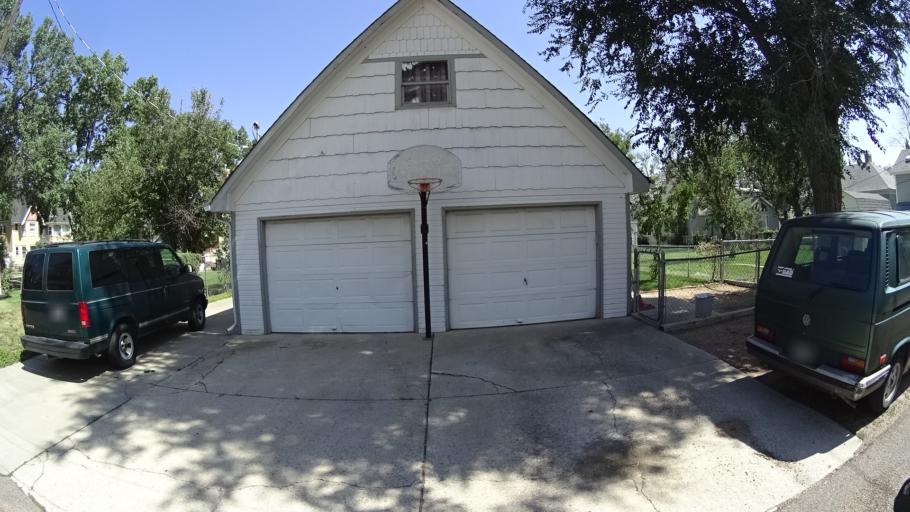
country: US
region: Colorado
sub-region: El Paso County
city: Colorado Springs
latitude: 38.8575
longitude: -104.8214
